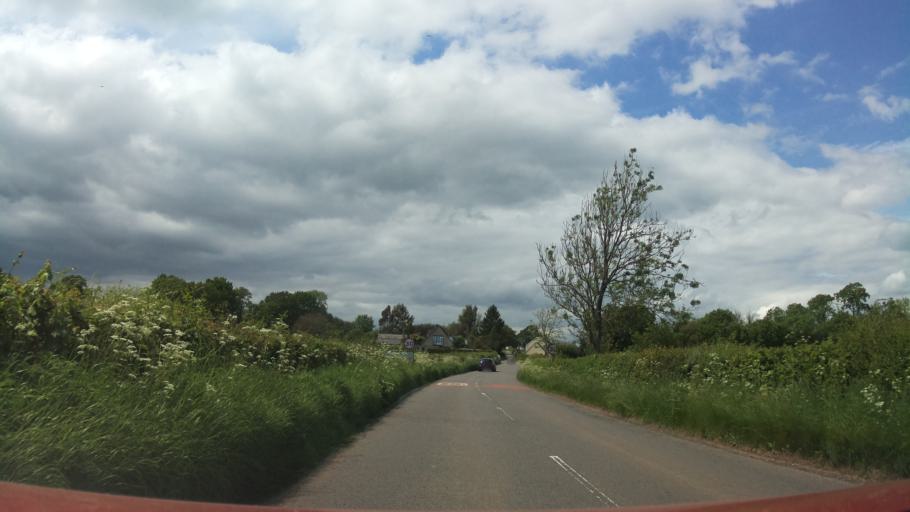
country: GB
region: England
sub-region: Herefordshire
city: Llanrothal
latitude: 51.8486
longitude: -2.7952
